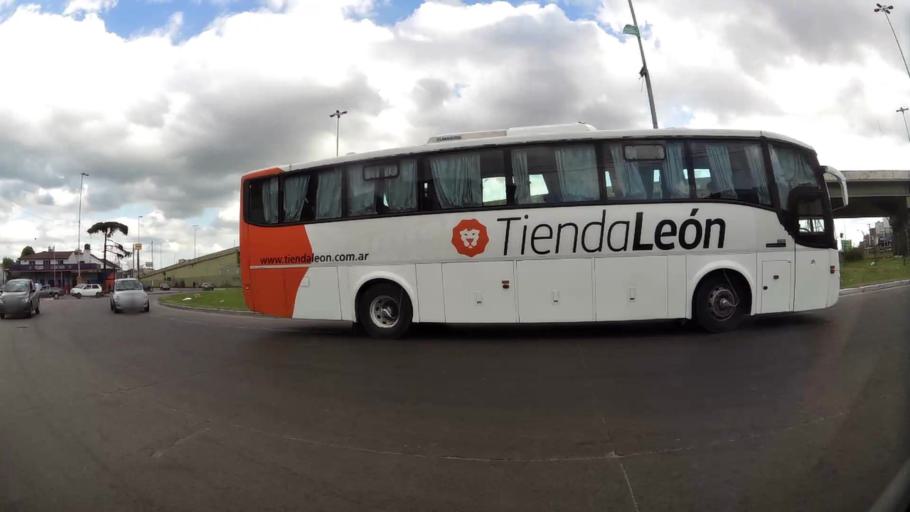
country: AR
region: Buenos Aires
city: San Justo
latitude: -34.6853
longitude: -58.5602
